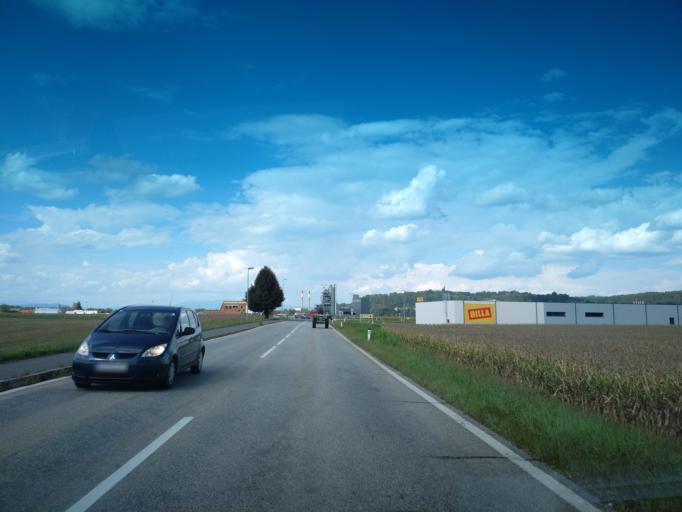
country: AT
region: Styria
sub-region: Politischer Bezirk Leibnitz
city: Weitendorf
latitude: 46.8847
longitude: 15.4892
